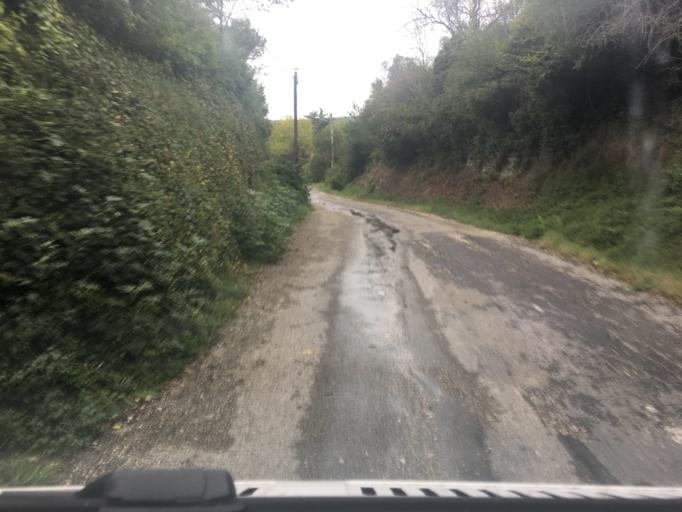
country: FR
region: Languedoc-Roussillon
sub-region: Departement du Gard
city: Uzes
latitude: 44.0203
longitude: 4.4091
